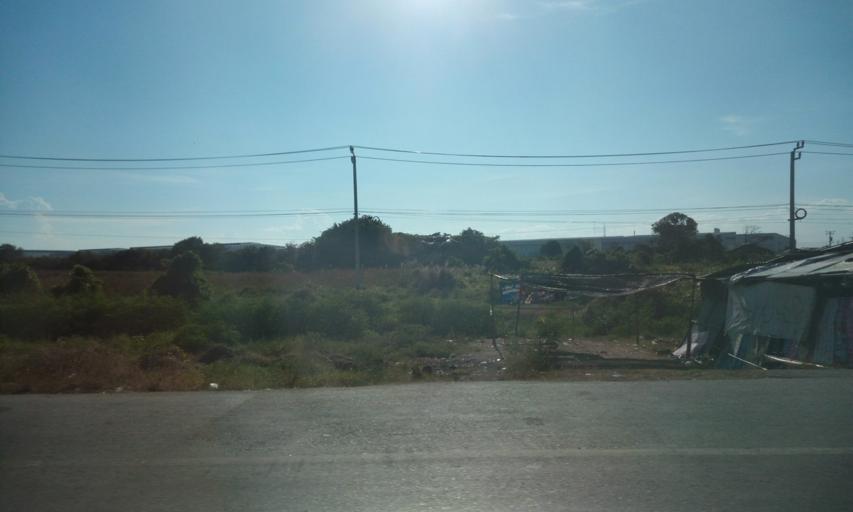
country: TH
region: Samut Prakan
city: Bang Bo District
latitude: 13.5759
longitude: 100.7572
